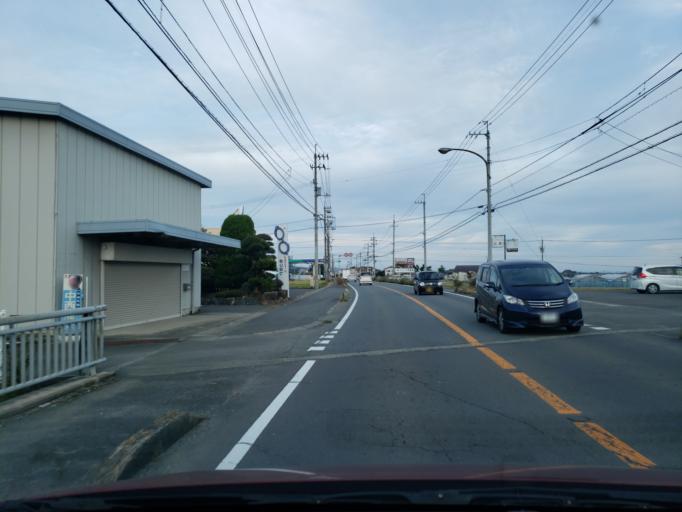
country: JP
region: Tokushima
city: Kamojimacho-jogejima
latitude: 34.0949
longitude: 134.3150
